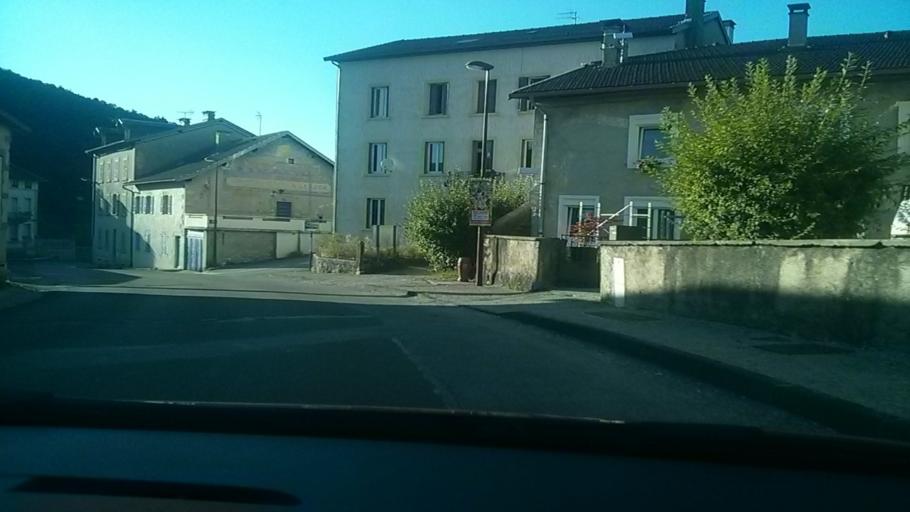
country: FR
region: Franche-Comte
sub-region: Departement du Jura
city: Saint-Claude
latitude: 46.3714
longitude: 5.8748
